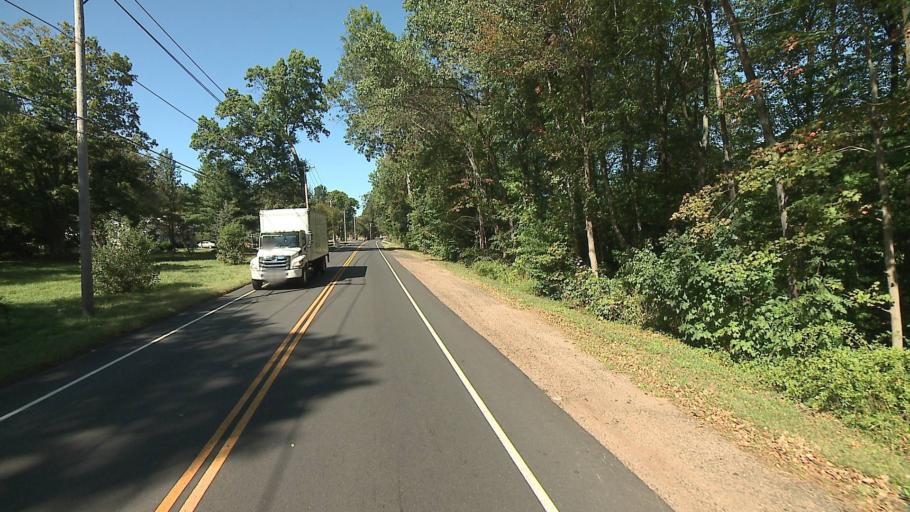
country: US
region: Connecticut
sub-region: New Haven County
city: Orange
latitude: 41.2759
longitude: -73.0060
